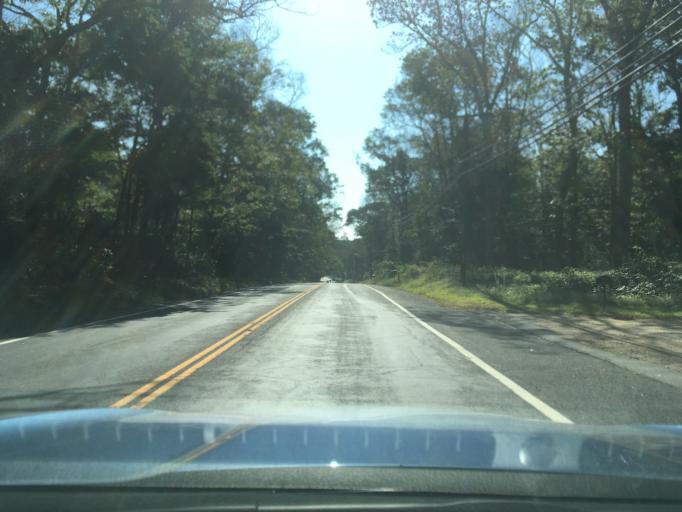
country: US
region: Rhode Island
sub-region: Washington County
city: Exeter
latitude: 41.5799
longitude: -71.5523
